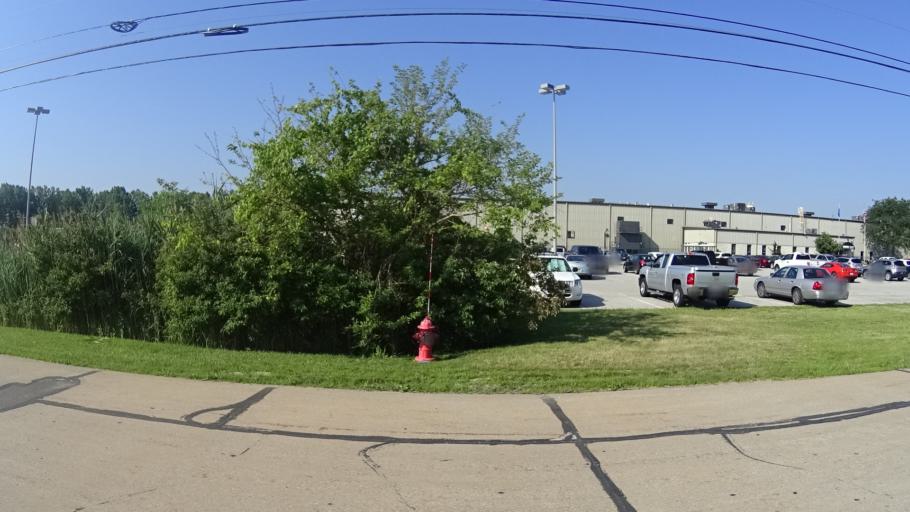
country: US
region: Ohio
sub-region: Erie County
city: Huron
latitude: 41.3982
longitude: -82.5805
